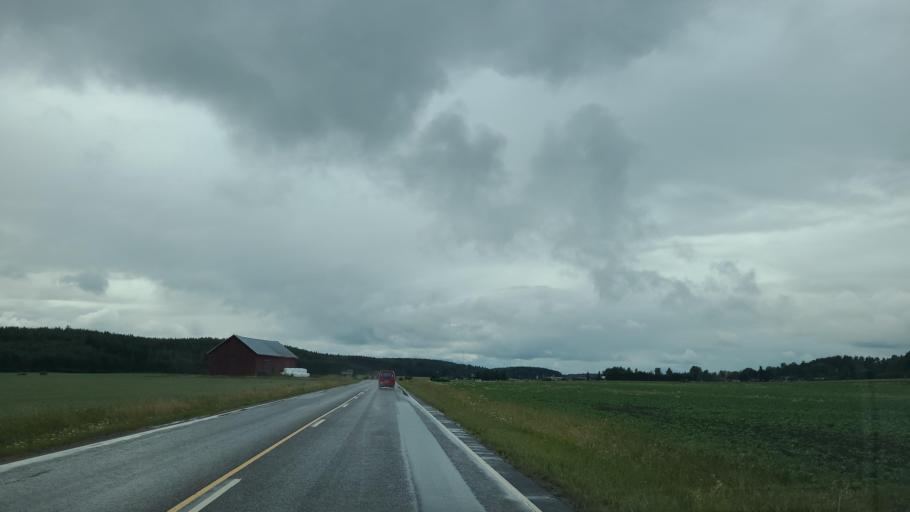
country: FI
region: Varsinais-Suomi
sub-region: Aboland-Turunmaa
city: Kimito
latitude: 60.1693
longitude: 22.7499
